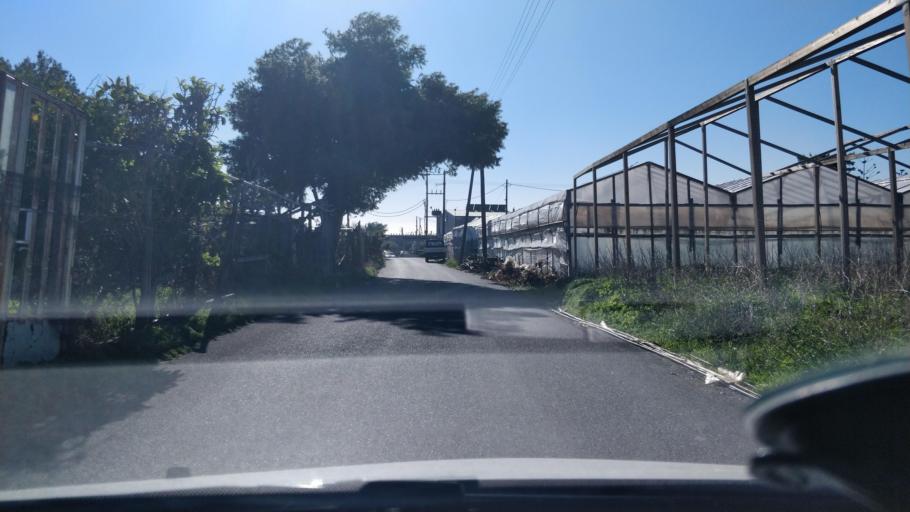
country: GR
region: Crete
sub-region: Nomos Lasithiou
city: Gra Liyia
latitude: 35.0161
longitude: 25.6764
